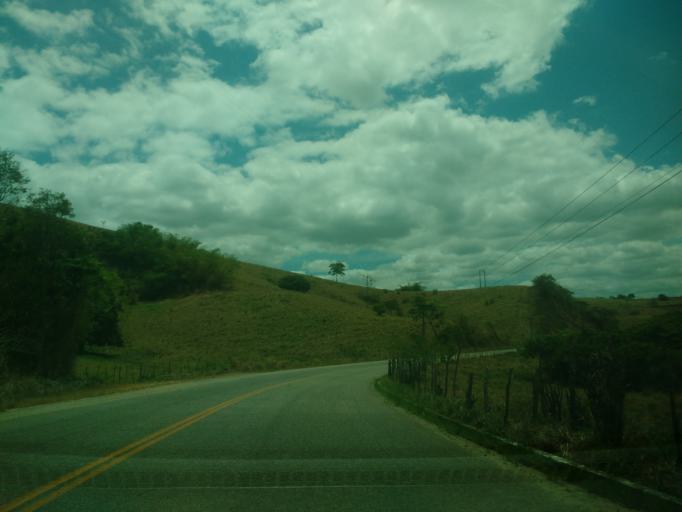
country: BR
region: Alagoas
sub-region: Santana Do Mundau
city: Santana do Mundau
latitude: -9.1443
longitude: -36.1631
